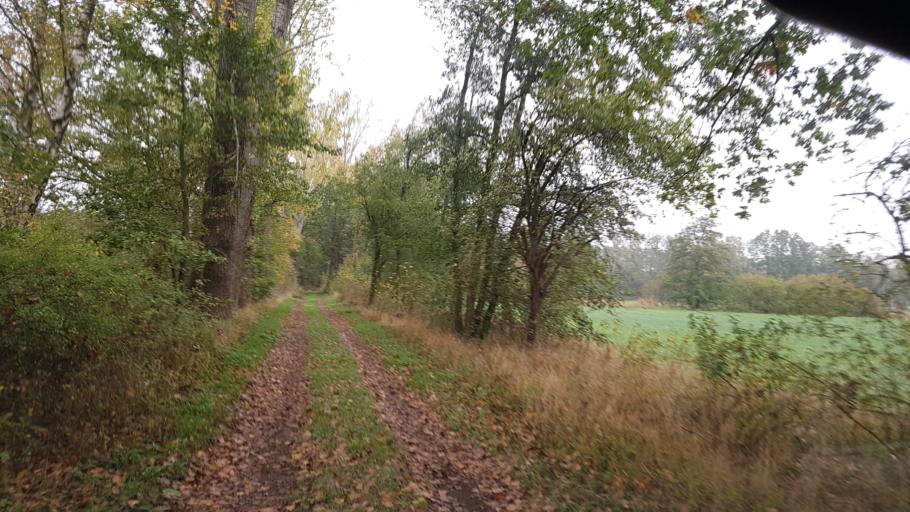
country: DE
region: Brandenburg
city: Schonewalde
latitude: 51.6914
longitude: 13.5997
